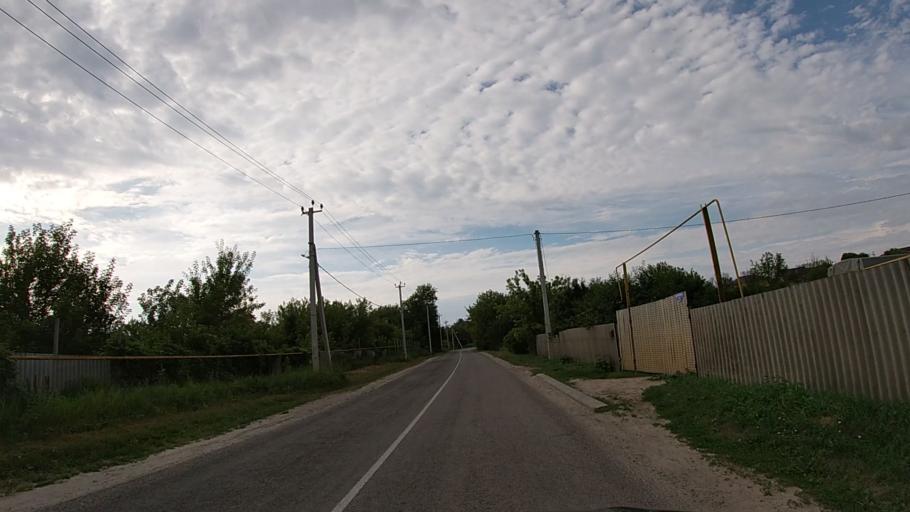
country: RU
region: Belgorod
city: Severnyy
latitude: 50.7091
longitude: 36.5992
